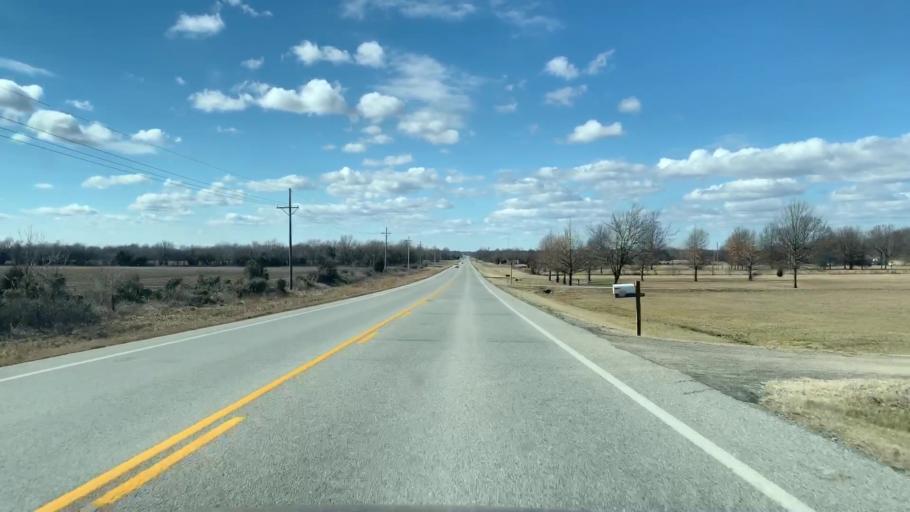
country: US
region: Kansas
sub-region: Cherokee County
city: Columbus
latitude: 37.1781
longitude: -94.7912
